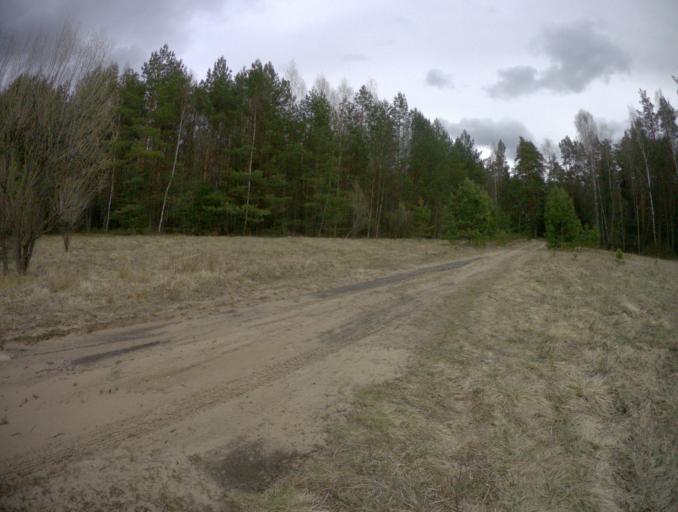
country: RU
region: Vladimir
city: Sudogda
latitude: 56.0611
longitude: 40.7967
